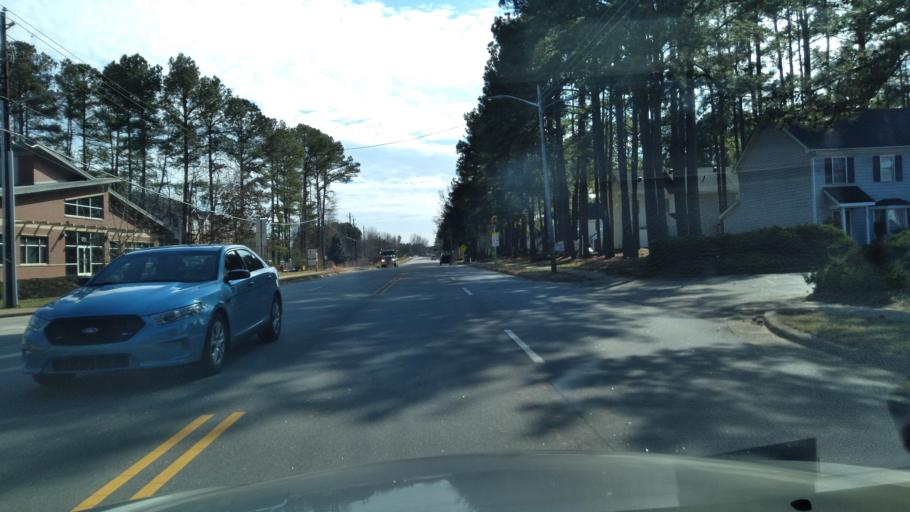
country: US
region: North Carolina
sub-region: Wake County
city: Garner
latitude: 35.6916
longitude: -78.6169
